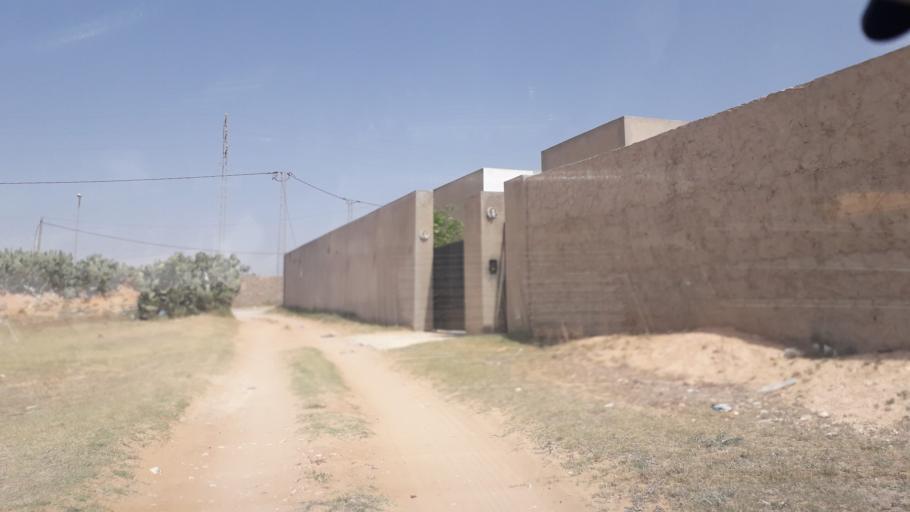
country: TN
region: Safaqis
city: Al Qarmadah
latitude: 34.8373
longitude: 10.7692
